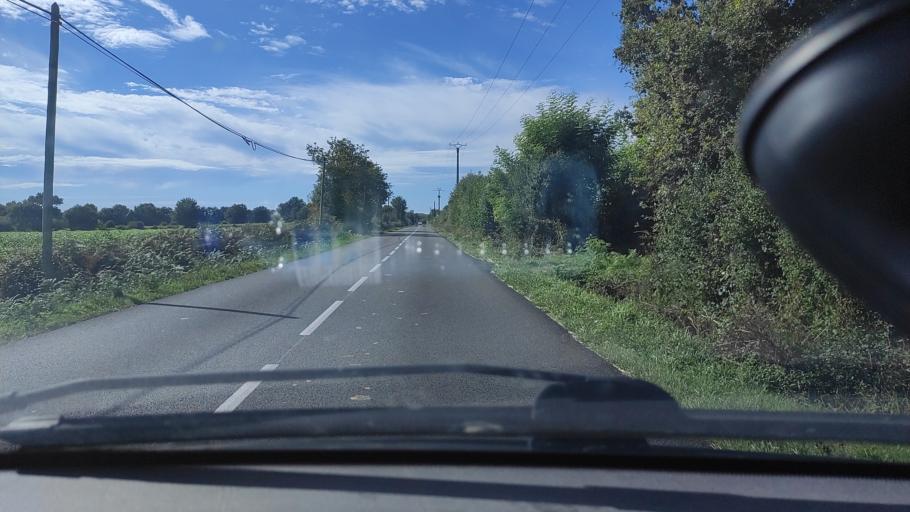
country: FR
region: Pays de la Loire
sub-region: Departement de la Vendee
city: La Boissiere-des-Landes
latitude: 46.5564
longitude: -1.4392
